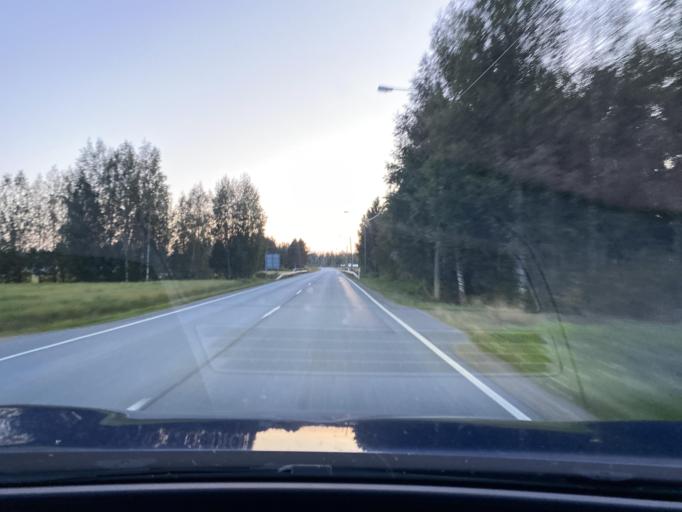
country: FI
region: Southern Ostrobothnia
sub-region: Seinaejoki
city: Kauhava
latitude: 63.1073
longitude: 23.0496
